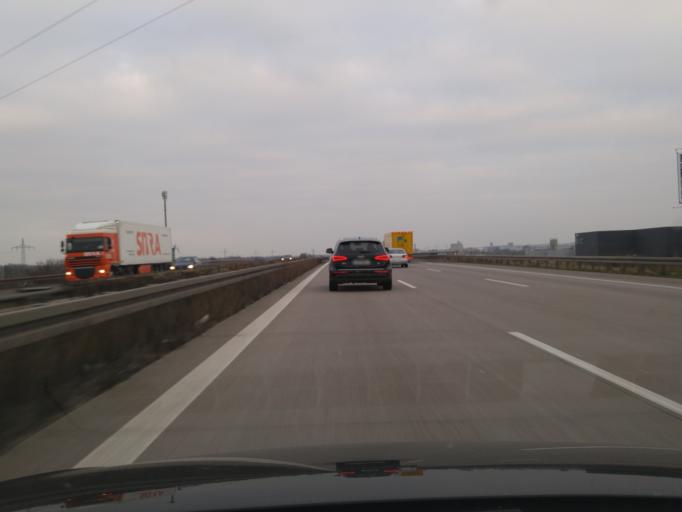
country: DE
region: Saxony-Anhalt
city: Barleben
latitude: 52.1993
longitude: 11.6441
